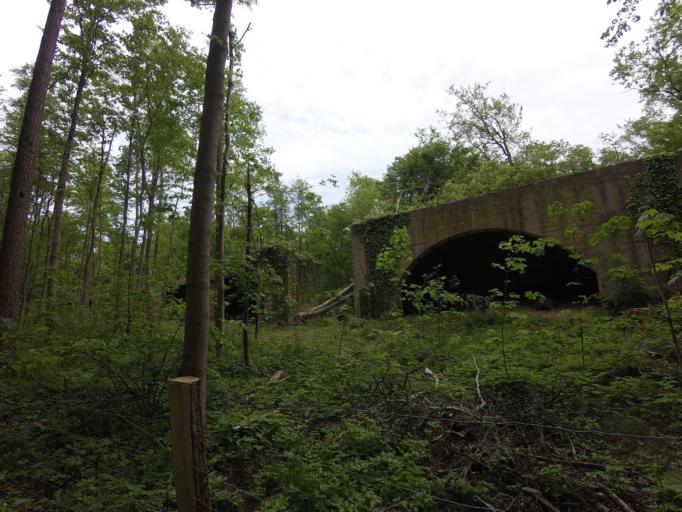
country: DE
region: Lower Saxony
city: Cremlingen
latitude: 52.2558
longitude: 10.6003
